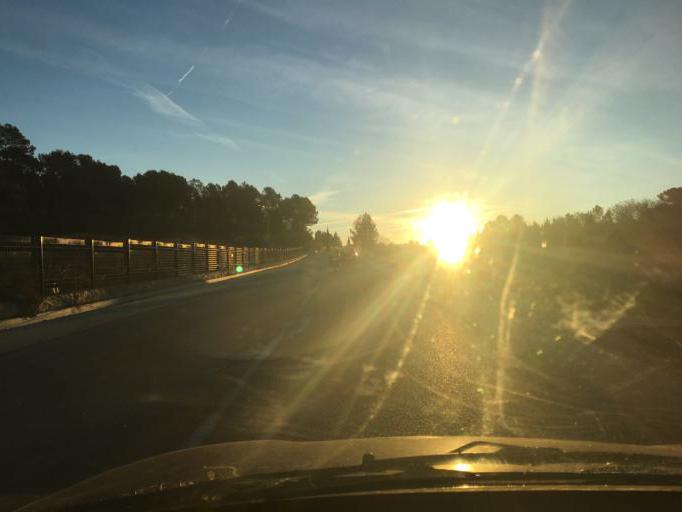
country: FR
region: Provence-Alpes-Cote d'Azur
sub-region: Departement du Var
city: Taradeau
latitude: 43.4664
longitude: 6.3908
